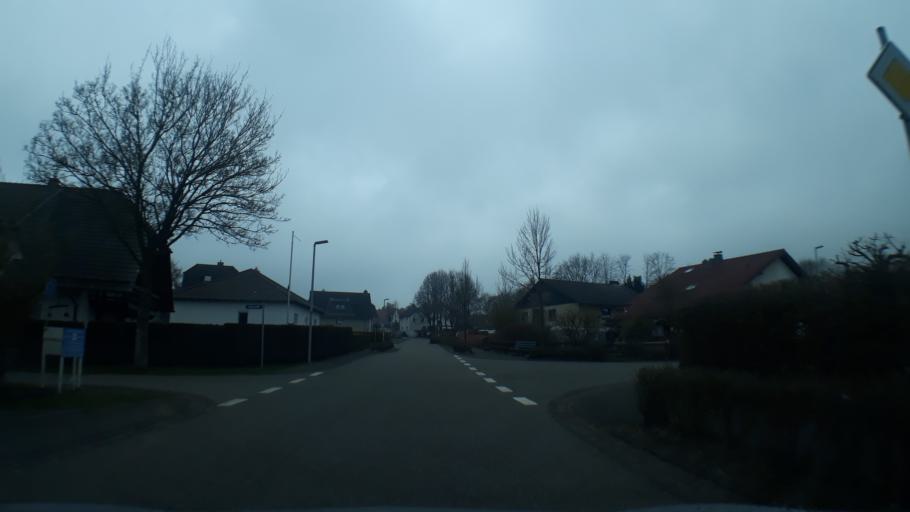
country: DE
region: North Rhine-Westphalia
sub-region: Regierungsbezirk Koln
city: Nettersheim
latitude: 50.4812
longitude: 6.5789
